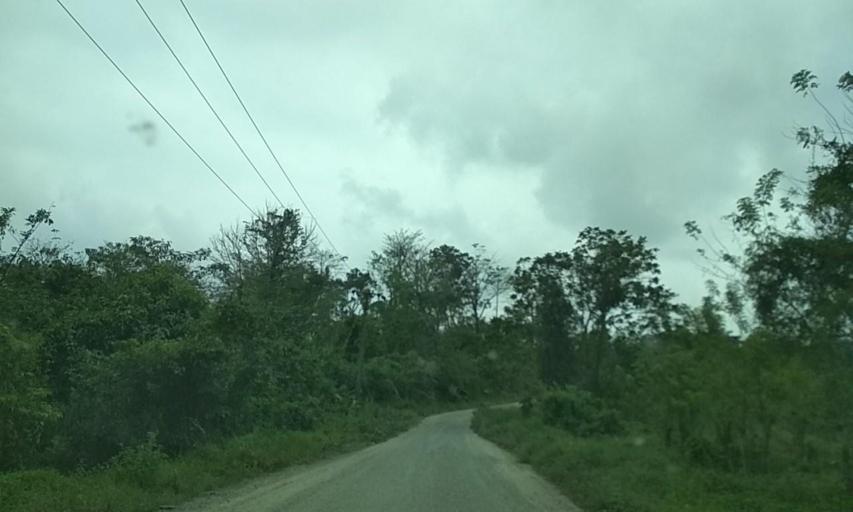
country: MX
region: Veracruz
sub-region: Uxpanapa
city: Poblado 10
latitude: 17.4846
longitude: -94.1274
